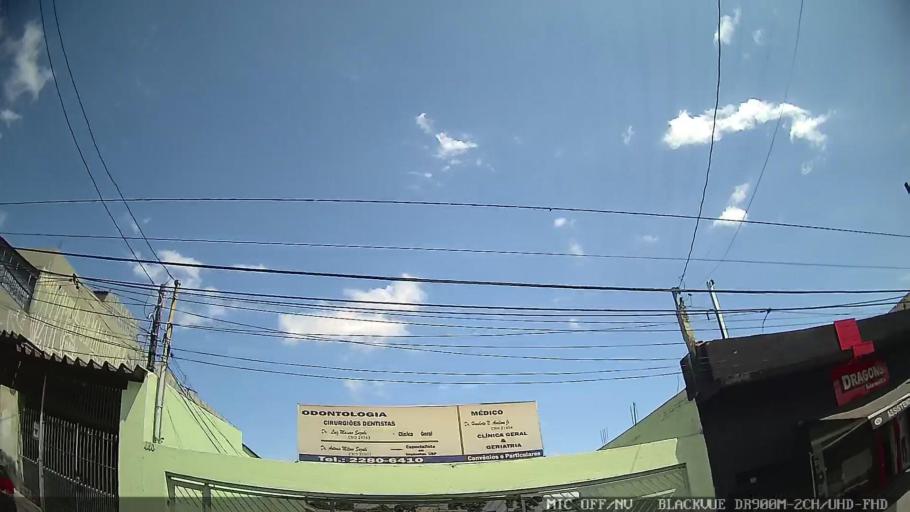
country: BR
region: Sao Paulo
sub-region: Guarulhos
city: Guarulhos
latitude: -23.5388
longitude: -46.4805
